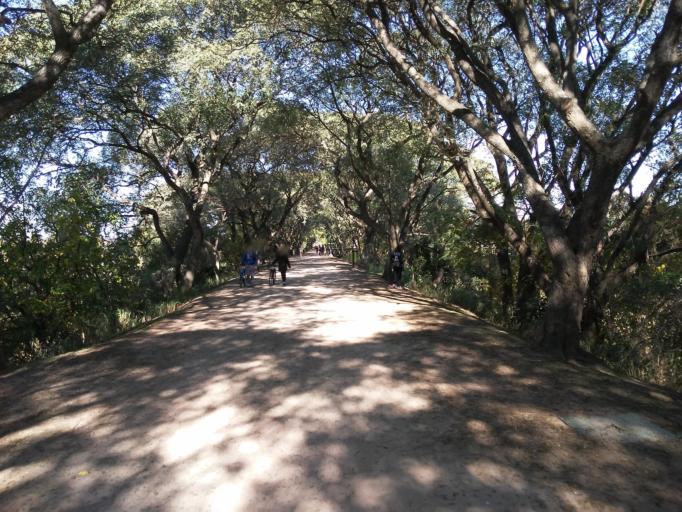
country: AR
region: Buenos Aires F.D.
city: Buenos Aires
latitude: -34.6115
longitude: -58.3567
